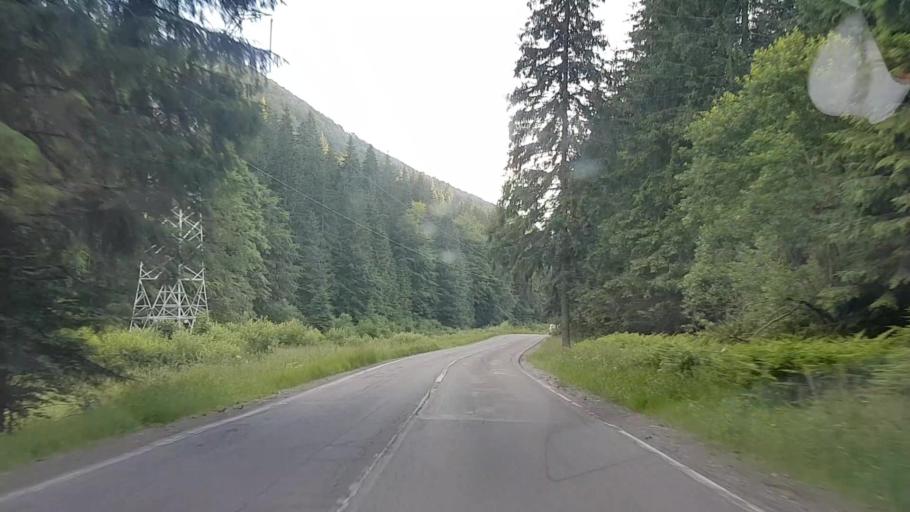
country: RO
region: Harghita
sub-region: Comuna Varsag
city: Varsag
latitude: 46.6318
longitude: 25.2644
